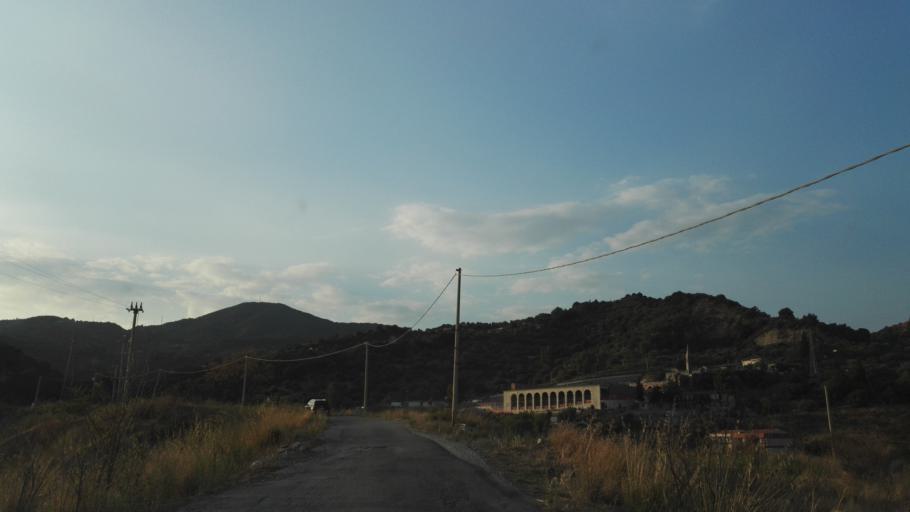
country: IT
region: Calabria
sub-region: Provincia di Reggio Calabria
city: Placanica
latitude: 38.4051
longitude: 16.4284
